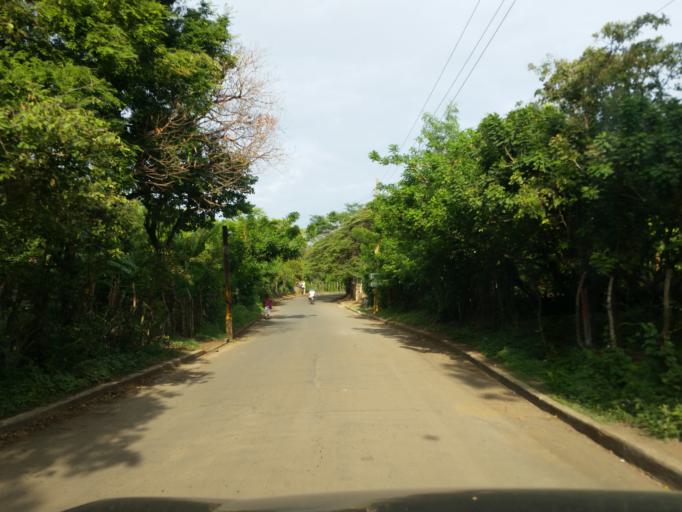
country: NI
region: Managua
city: Managua
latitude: 12.1068
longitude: -86.2179
